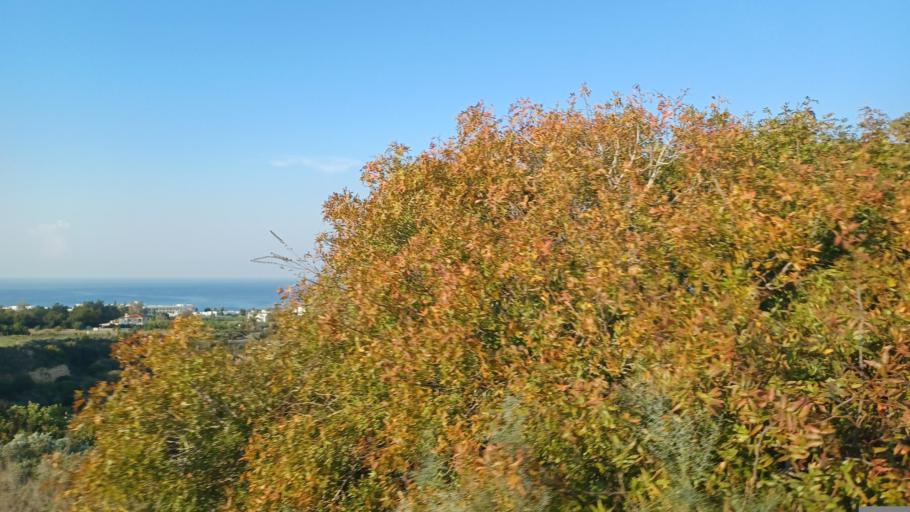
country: CY
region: Pafos
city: Kissonerga
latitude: 34.8312
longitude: 32.3988
